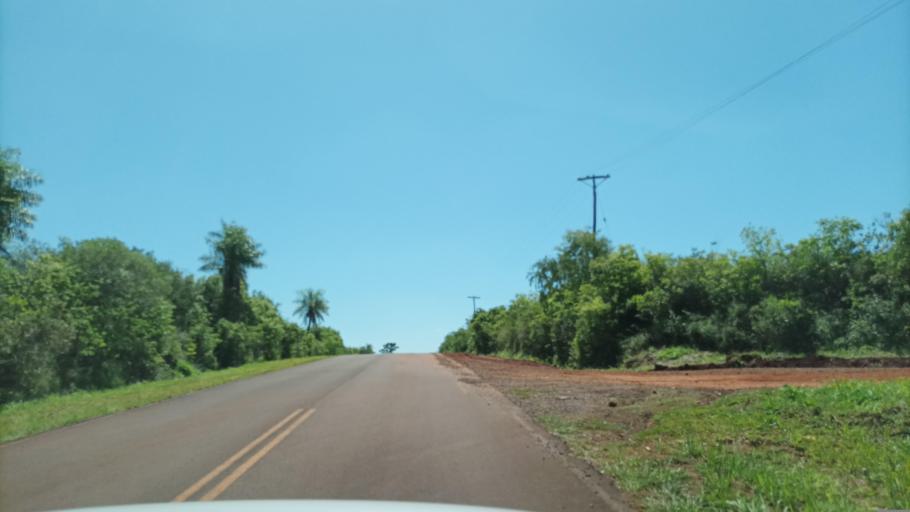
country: AR
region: Misiones
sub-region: Departamento de Apostoles
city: San Jose
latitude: -27.7734
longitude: -55.7522
